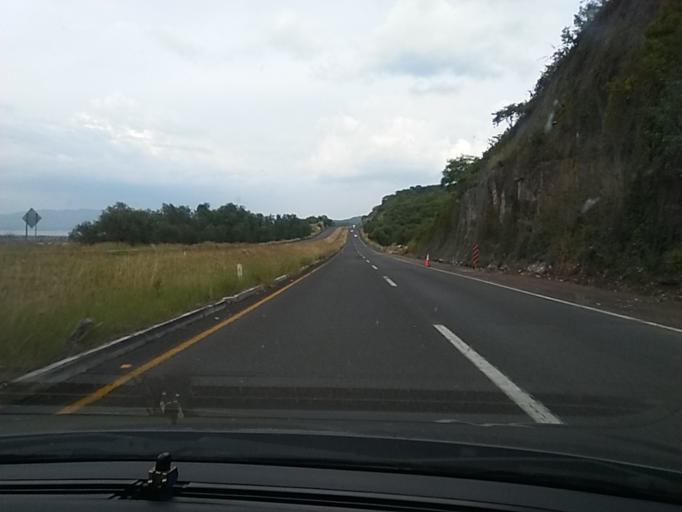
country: MX
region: Mexico
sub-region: Chapultepec
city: Chucandiro
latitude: 19.8838
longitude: -101.3391
